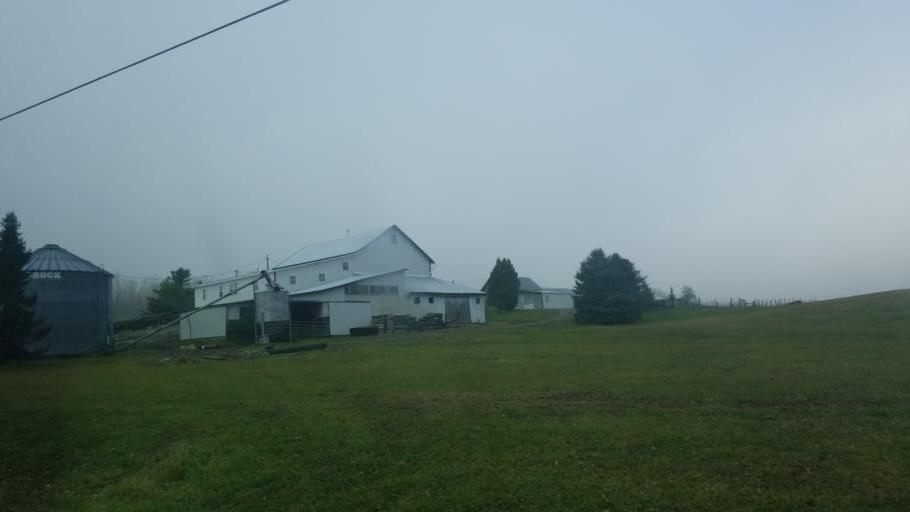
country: US
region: Ohio
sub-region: Champaign County
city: North Lewisburg
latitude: 40.2851
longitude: -83.6102
